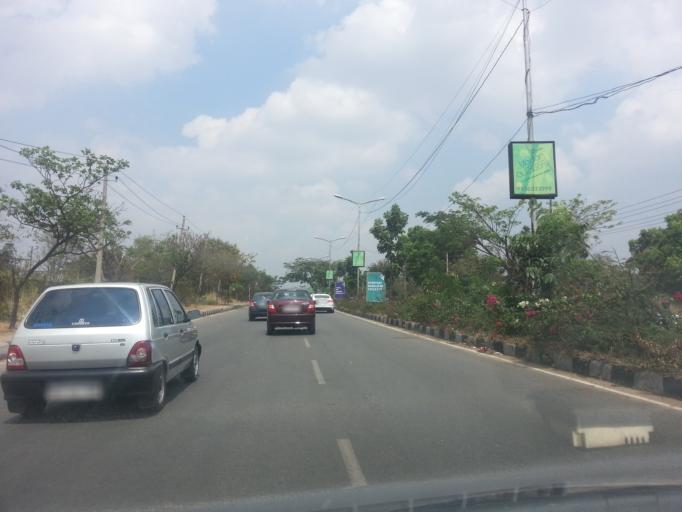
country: IN
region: Karnataka
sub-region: Bangalore Urban
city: Bangalore
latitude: 12.9448
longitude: 77.6393
